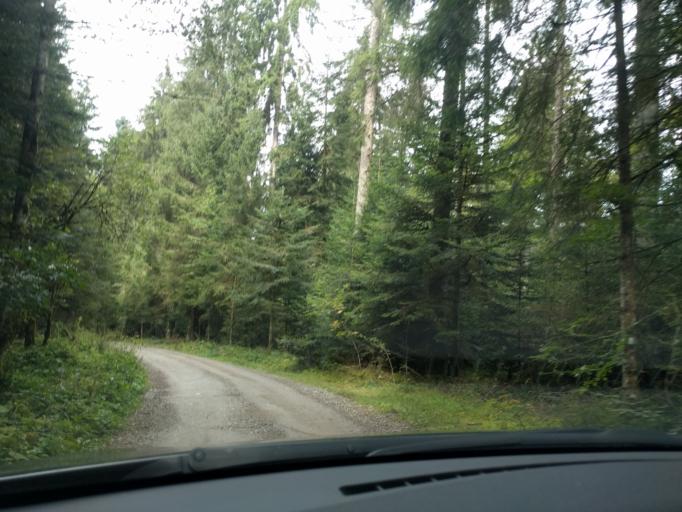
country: CH
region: Bern
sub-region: Bern-Mittelland District
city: Linden
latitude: 46.8617
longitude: 7.6528
